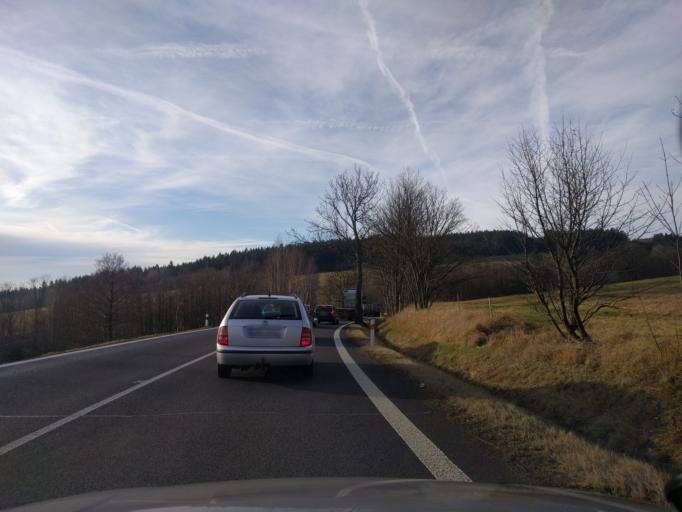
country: CZ
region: Liberecky
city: Mnisek
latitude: 50.8578
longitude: 15.0307
